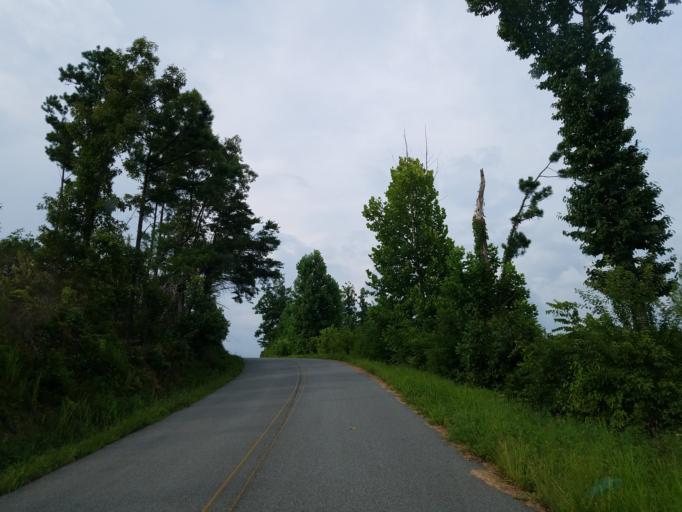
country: US
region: Georgia
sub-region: Bartow County
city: Rydal
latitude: 34.3910
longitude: -84.6669
